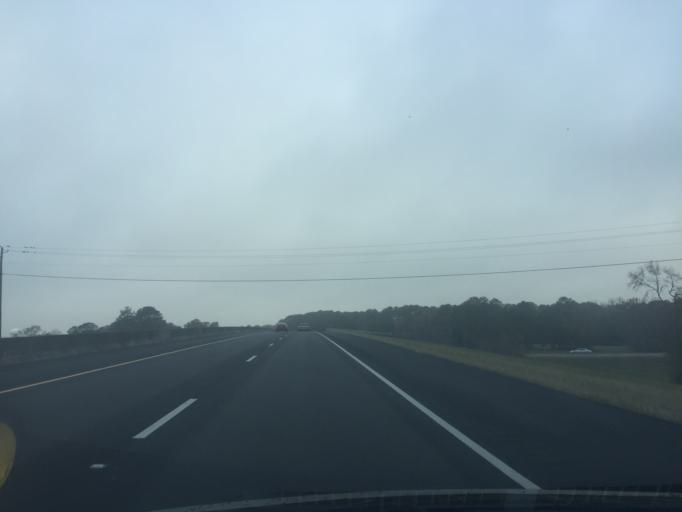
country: US
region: Georgia
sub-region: Chatham County
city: Georgetown
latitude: 31.9994
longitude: -81.2467
